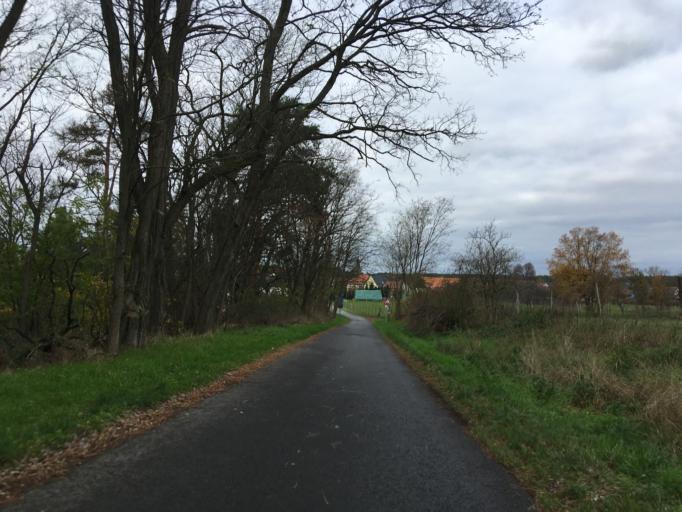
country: DE
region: Brandenburg
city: Jamlitz
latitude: 52.0878
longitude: 14.4352
